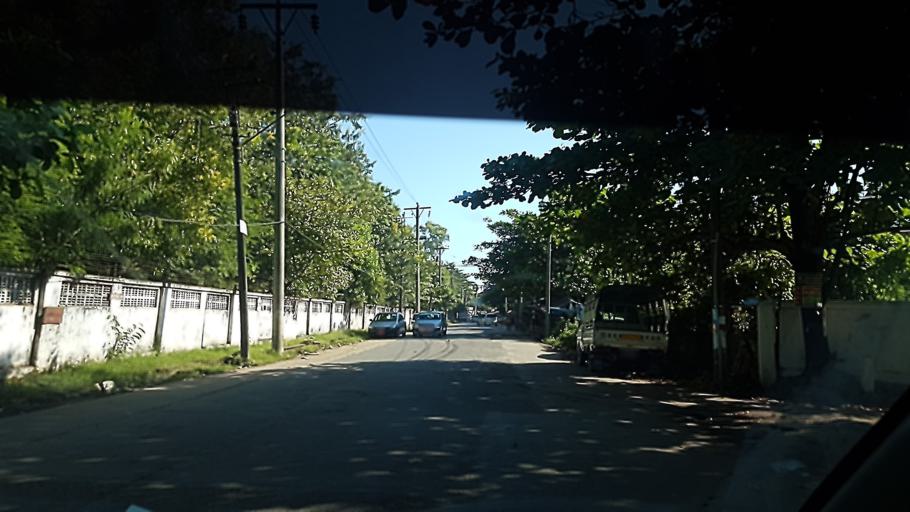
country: MM
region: Yangon
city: Yangon
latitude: 16.8536
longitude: 96.1143
